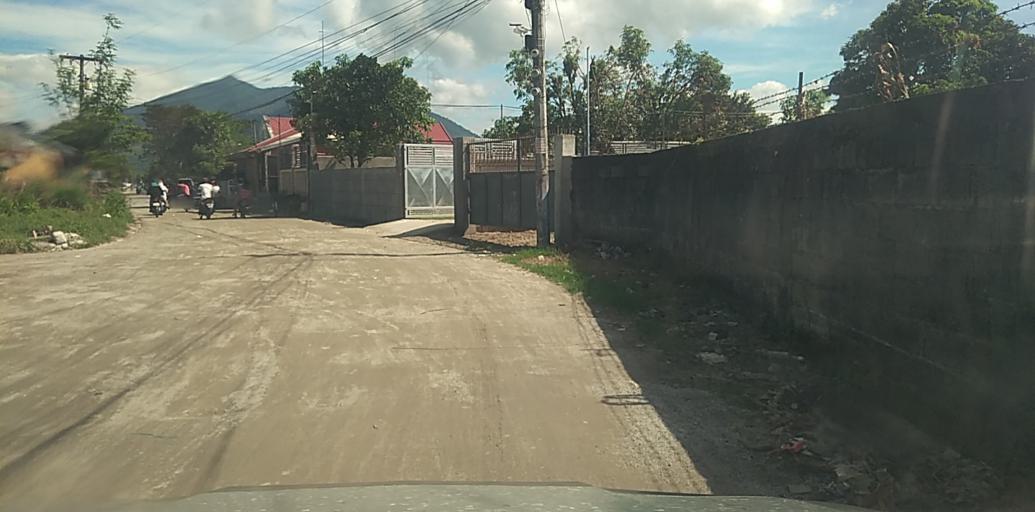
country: PH
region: Central Luzon
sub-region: Province of Pampanga
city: Buensuseso
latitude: 15.1924
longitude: 120.6664
